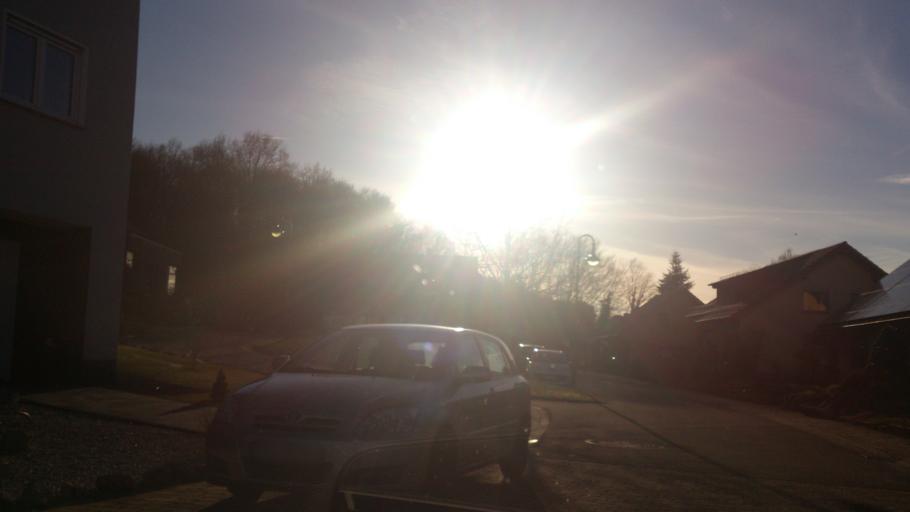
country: DE
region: Saarland
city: Mainzweiler
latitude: 49.3942
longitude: 7.0905
